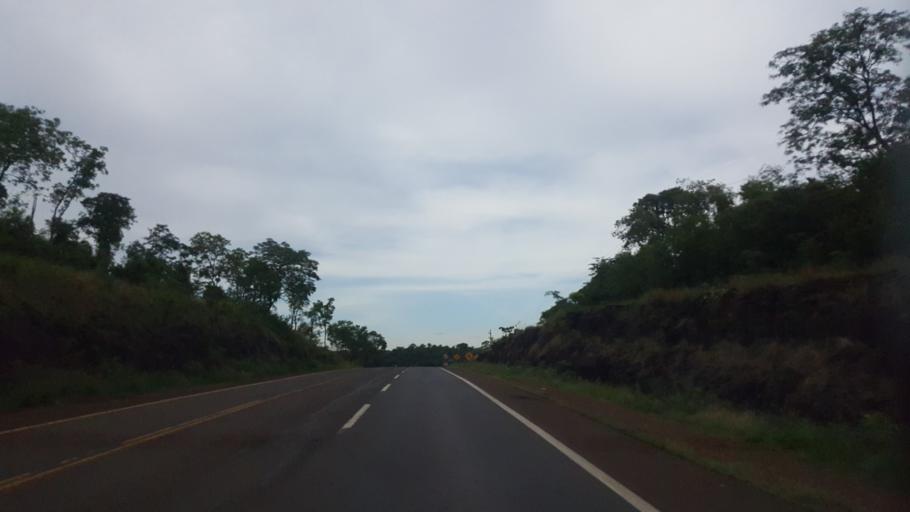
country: AR
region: Misiones
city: Santa Ana
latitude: -27.3565
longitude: -55.5553
